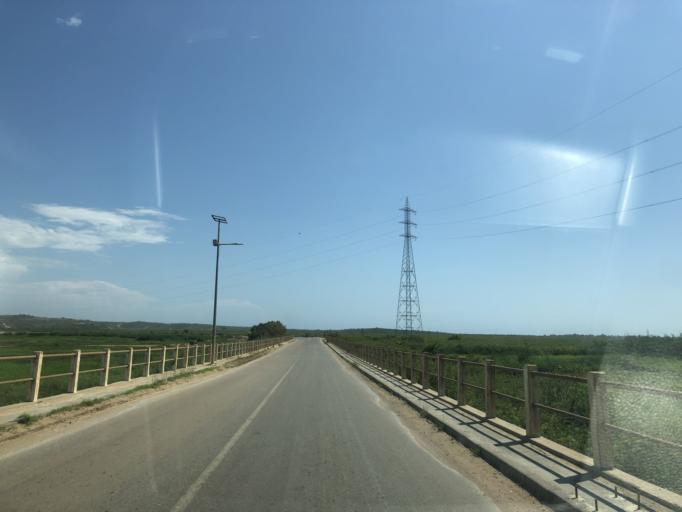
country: AO
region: Cuanza Sul
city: Sumbe
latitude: -10.8754
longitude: 13.8396
